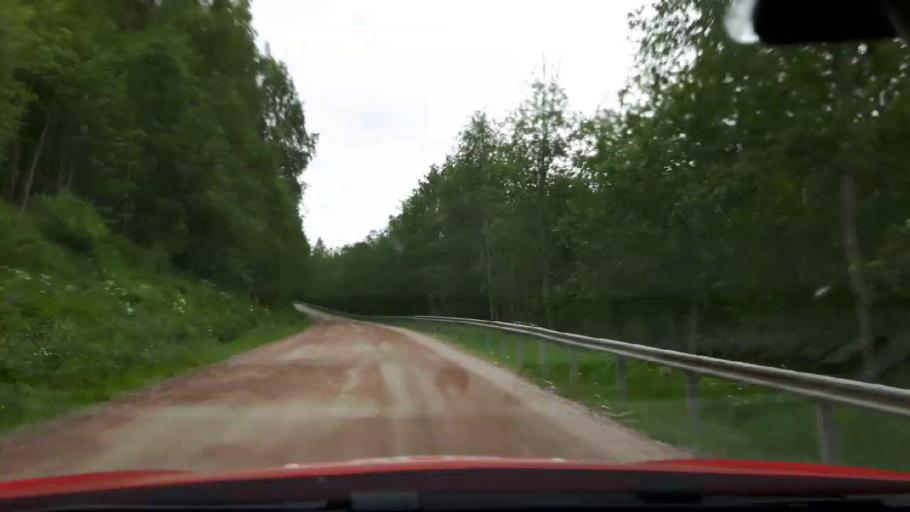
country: SE
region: Jaemtland
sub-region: Ragunda Kommun
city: Hammarstrand
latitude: 63.1909
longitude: 16.1378
